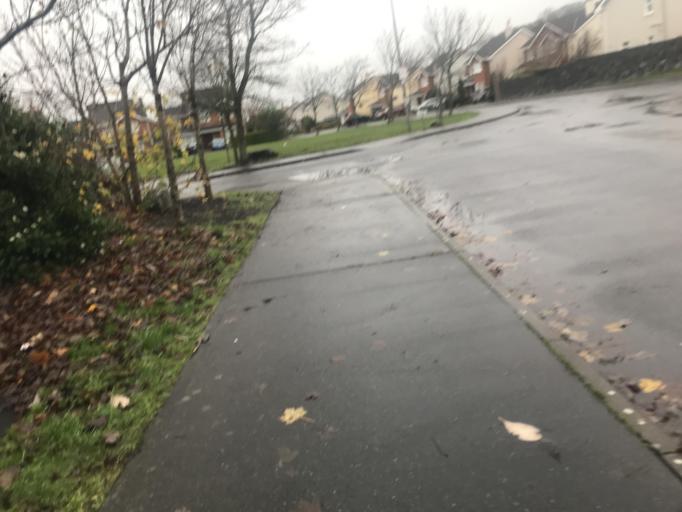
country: IE
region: Connaught
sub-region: County Galway
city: Oranmore
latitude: 53.2628
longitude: -8.9339
